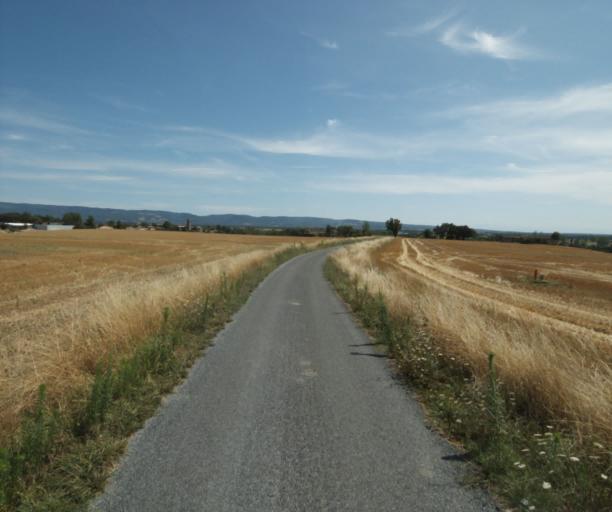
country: FR
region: Midi-Pyrenees
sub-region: Departement du Tarn
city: Puylaurens
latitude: 43.5326
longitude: 2.0030
